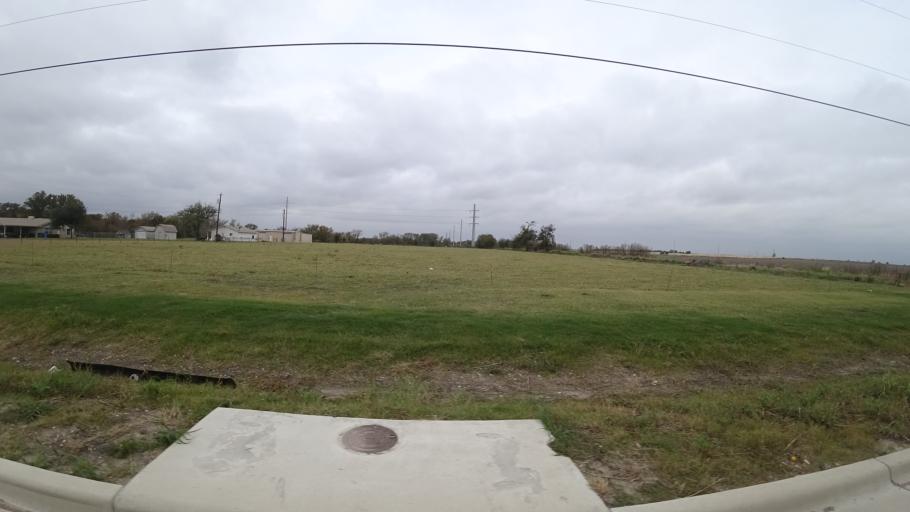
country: US
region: Texas
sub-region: Travis County
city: Pflugerville
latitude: 30.4268
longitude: -97.5749
